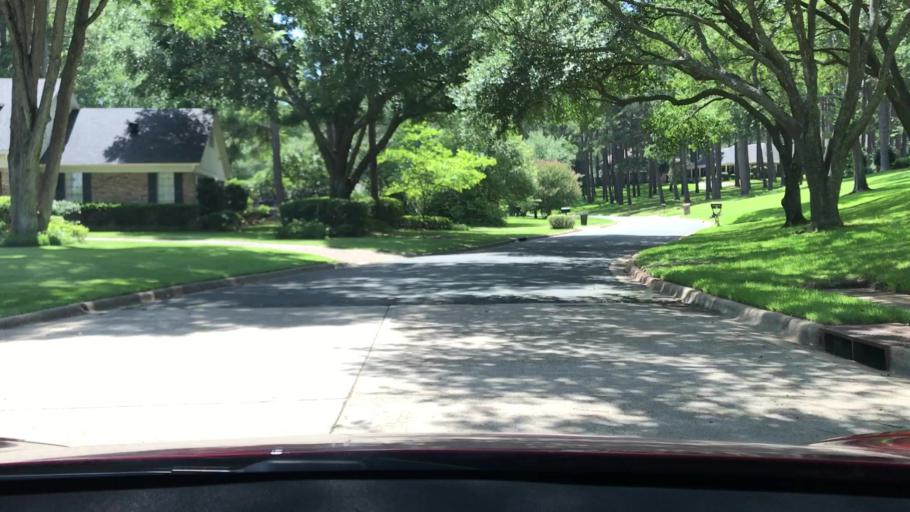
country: US
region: Louisiana
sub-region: Bossier Parish
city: Bossier City
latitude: 32.4329
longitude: -93.7284
